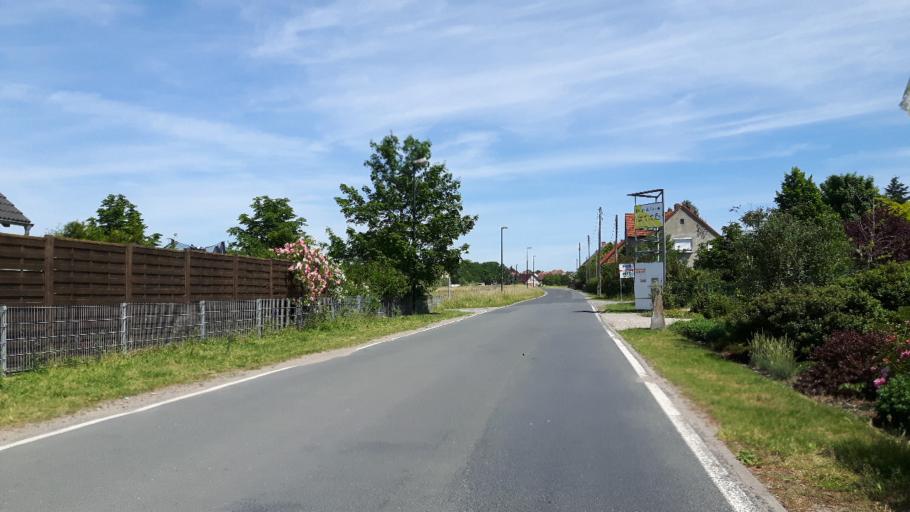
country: DE
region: Saxony-Anhalt
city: Wittenburg
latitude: 51.8934
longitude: 12.6426
